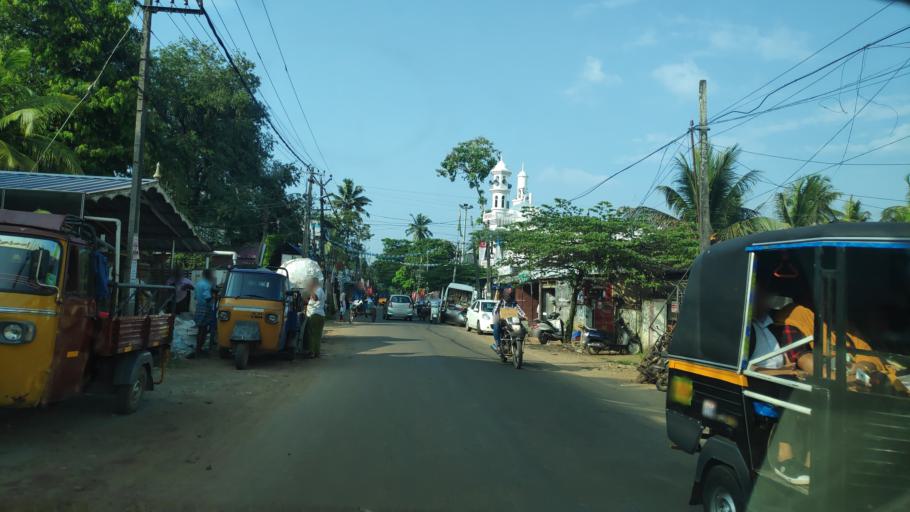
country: IN
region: Kerala
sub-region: Alappuzha
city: Alleppey
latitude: 9.4846
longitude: 76.3339
